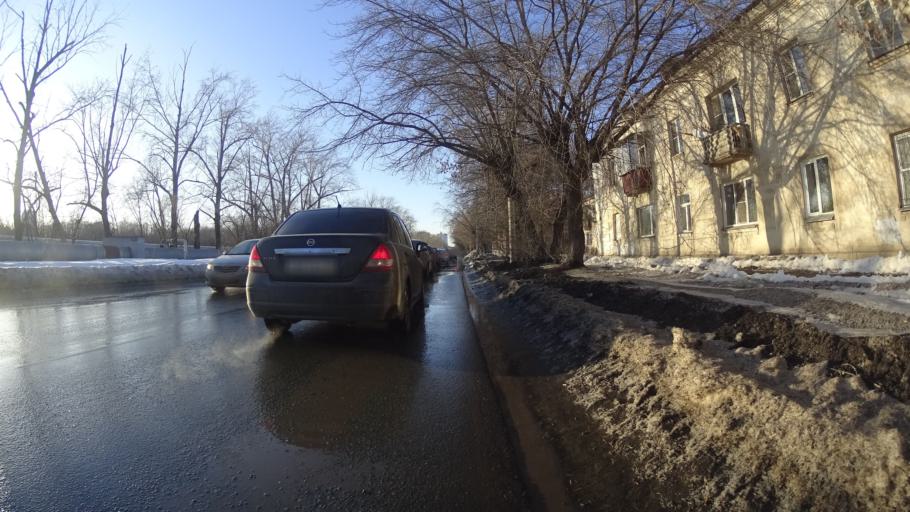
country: RU
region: Chelyabinsk
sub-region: Gorod Chelyabinsk
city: Chelyabinsk
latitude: 55.1324
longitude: 61.4619
